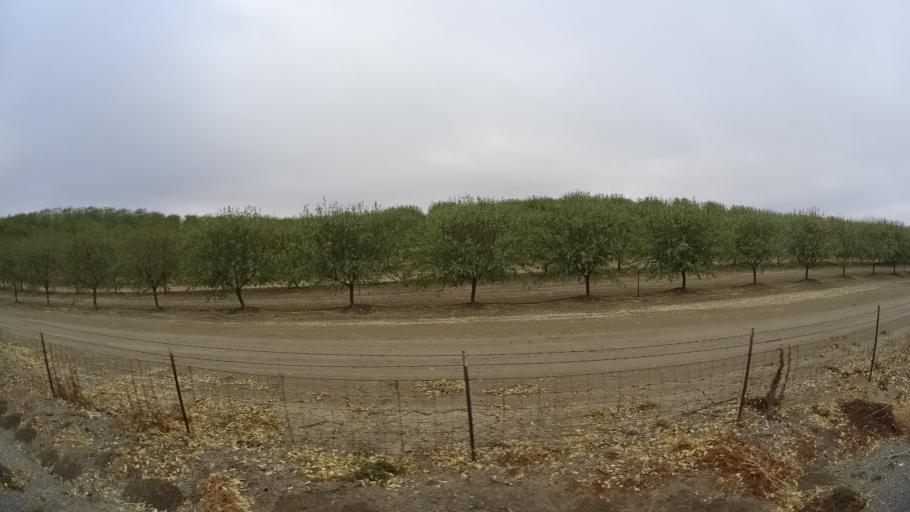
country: US
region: California
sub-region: Yolo County
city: Dunnigan
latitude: 38.8790
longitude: -122.0259
